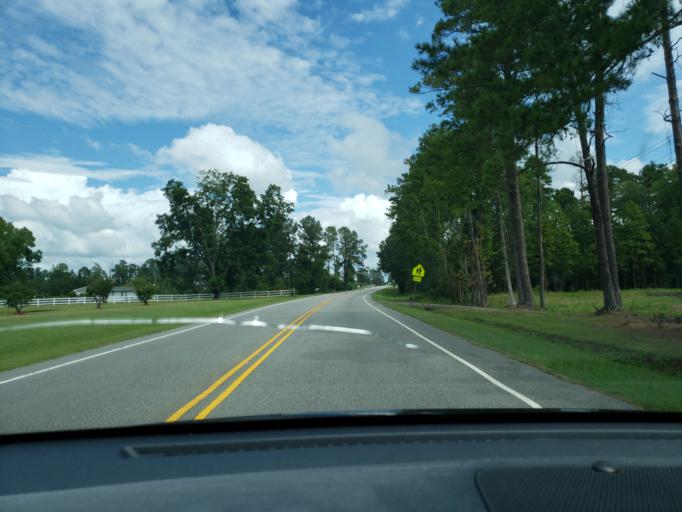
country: US
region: North Carolina
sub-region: Columbus County
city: Brunswick
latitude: 34.1997
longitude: -78.7657
